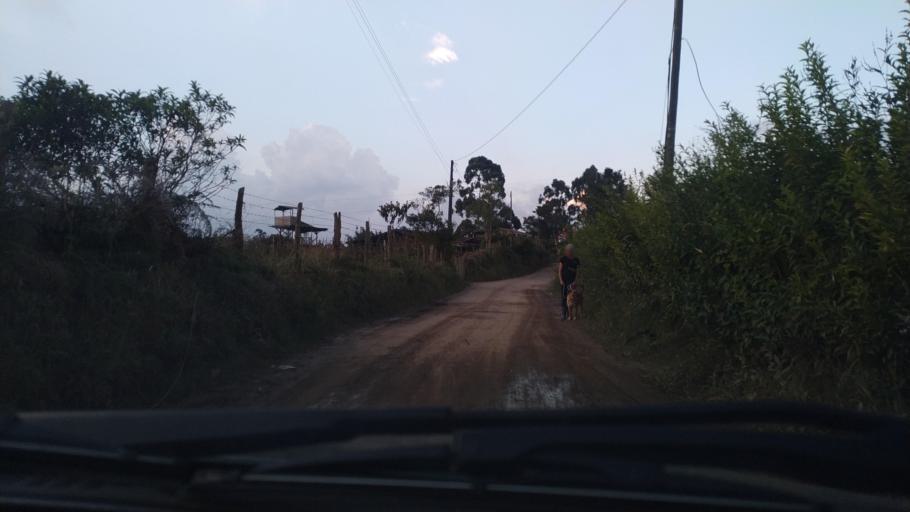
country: CO
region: Antioquia
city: Marinilla
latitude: 6.1916
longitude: -75.2830
